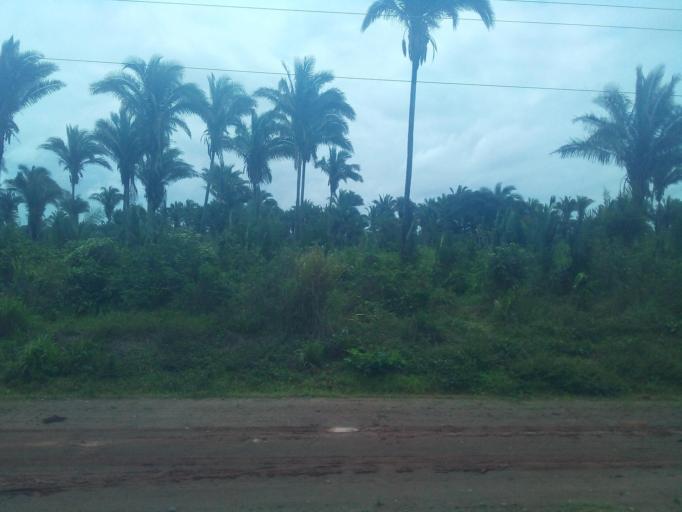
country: BR
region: Maranhao
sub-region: Vitoria Do Mearim
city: Vitoria do Mearim
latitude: -3.5654
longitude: -44.9236
